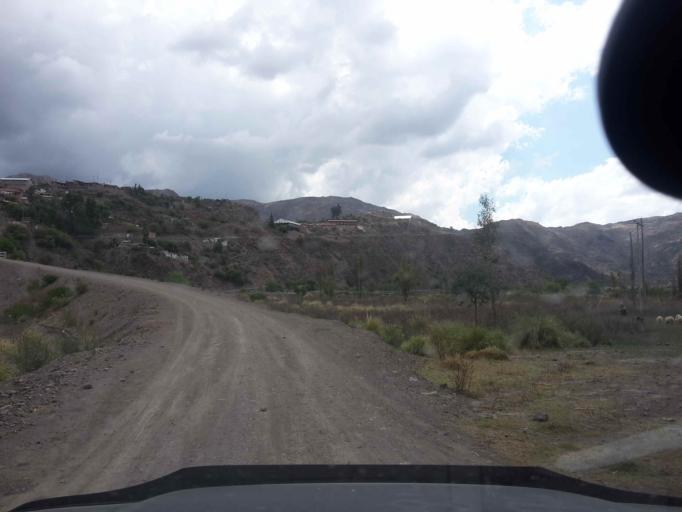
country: BO
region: Cochabamba
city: Colchani
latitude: -17.5146
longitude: -66.6169
